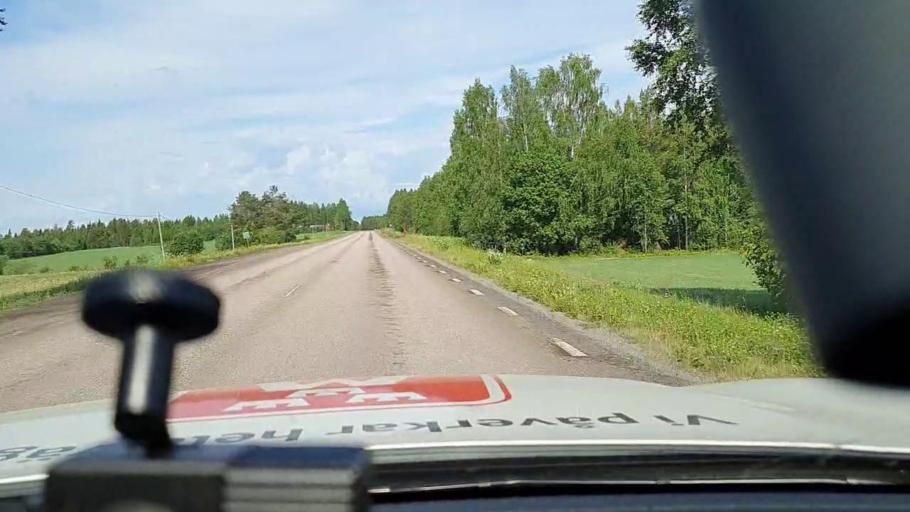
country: SE
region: Norrbotten
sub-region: Alvsbyns Kommun
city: AElvsbyn
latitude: 66.0181
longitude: 21.1488
